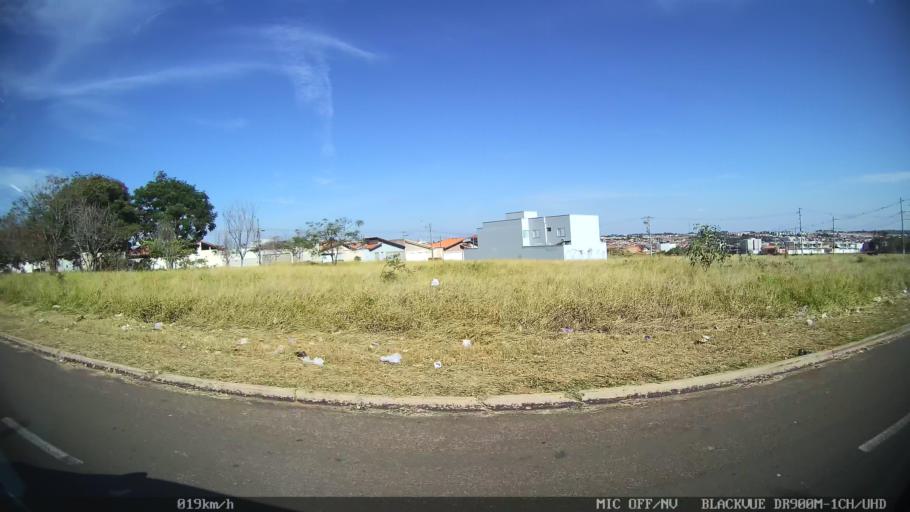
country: BR
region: Sao Paulo
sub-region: Franca
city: Franca
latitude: -20.5089
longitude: -47.4284
